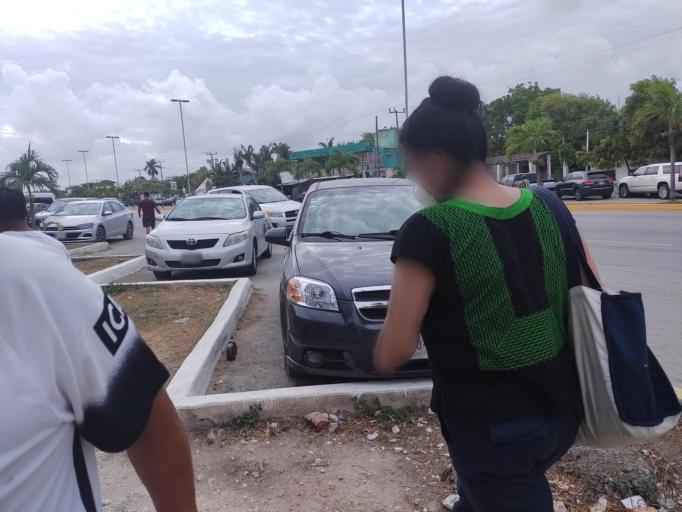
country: MX
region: Quintana Roo
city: Tulum
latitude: 20.2092
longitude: -87.4686
